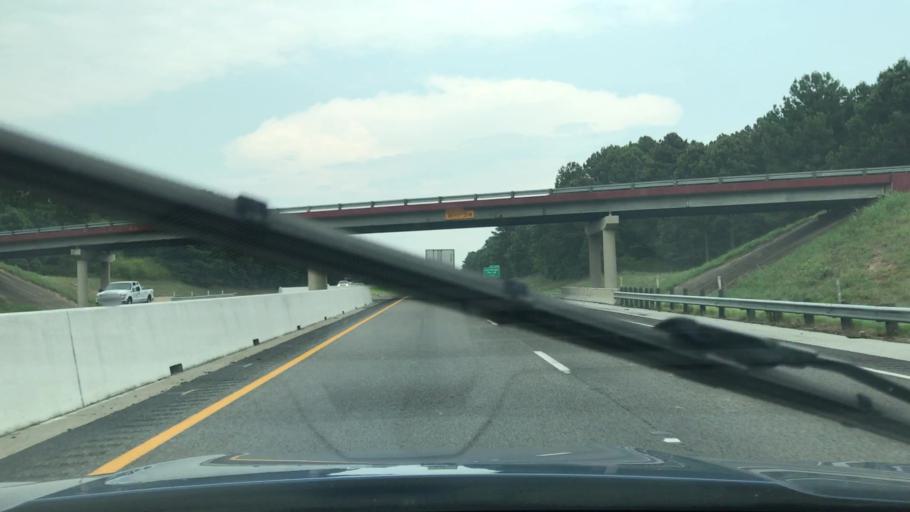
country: US
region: Texas
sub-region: Gregg County
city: Liberty City
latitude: 32.4370
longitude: -95.0121
